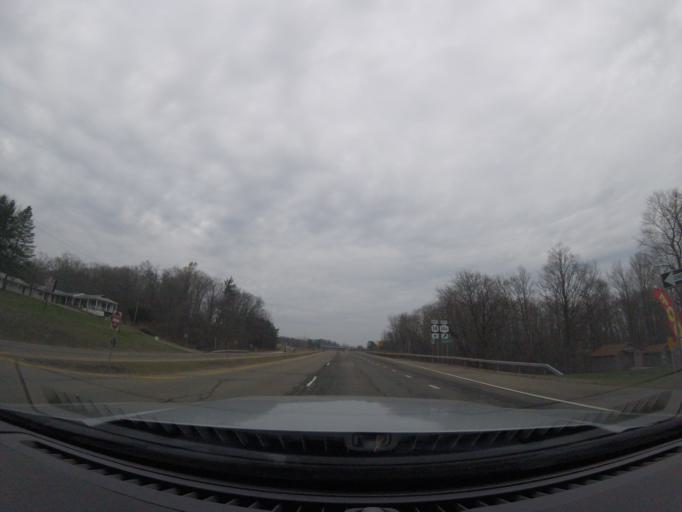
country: US
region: New York
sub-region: Schuyler County
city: Watkins Glen
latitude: 42.4179
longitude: -76.9024
